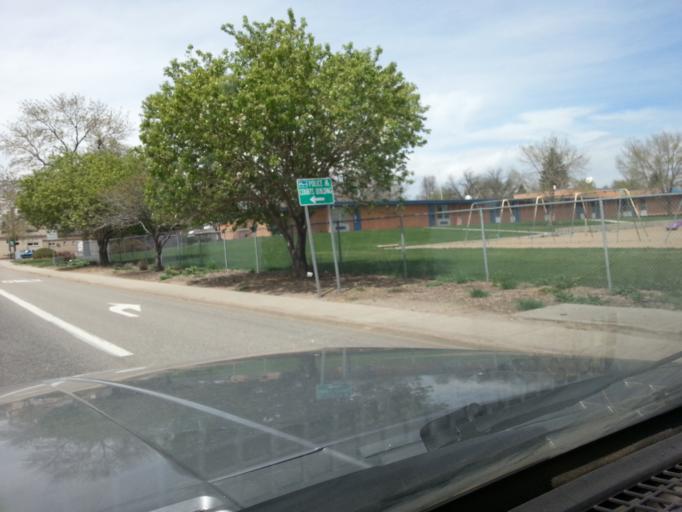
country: US
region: Colorado
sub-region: Larimer County
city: Loveland
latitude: 40.4074
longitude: -105.0669
